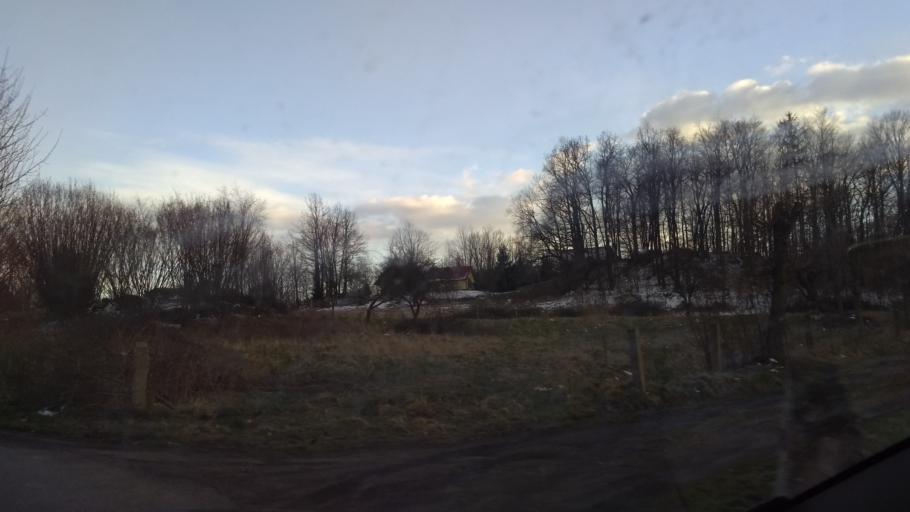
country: PL
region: Lower Silesian Voivodeship
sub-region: Powiat jeleniogorski
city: Sosnowka
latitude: 50.8452
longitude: 15.7373
